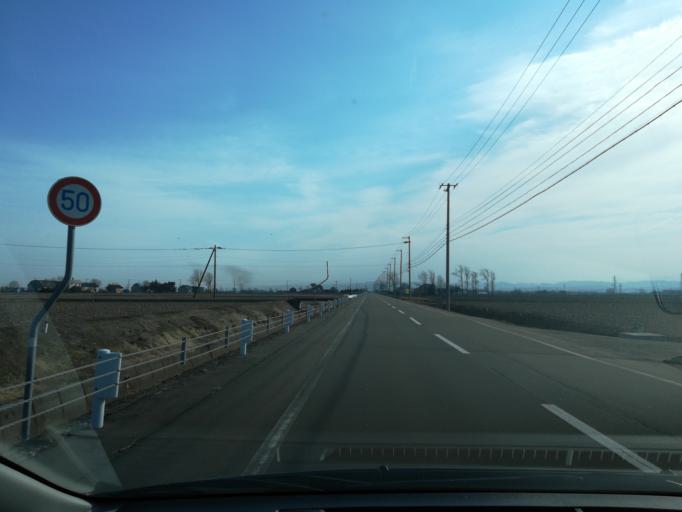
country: JP
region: Hokkaido
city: Iwamizawa
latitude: 43.1755
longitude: 141.6781
